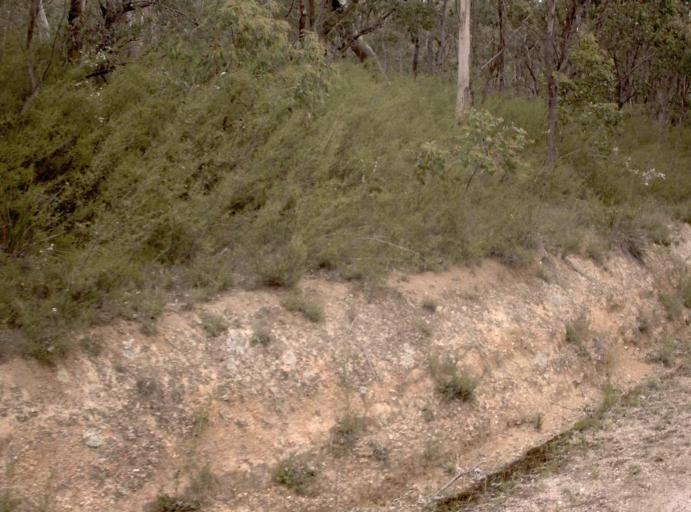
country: AU
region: Victoria
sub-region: East Gippsland
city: Bairnsdale
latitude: -37.6359
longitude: 147.2428
